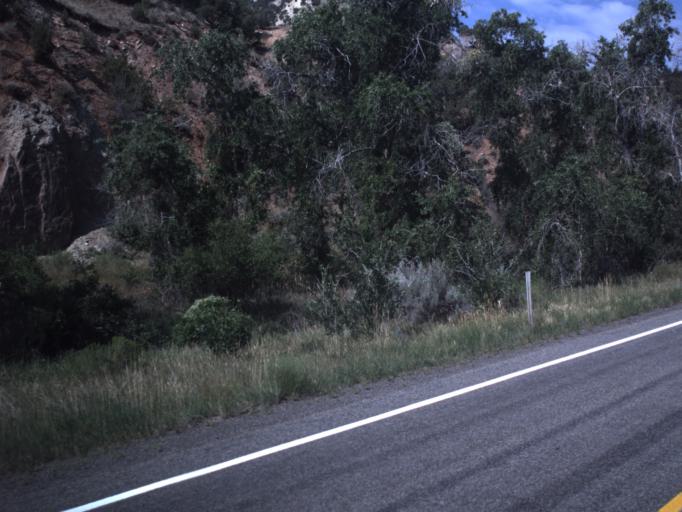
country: US
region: Utah
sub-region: Daggett County
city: Manila
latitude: 40.9266
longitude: -109.7182
